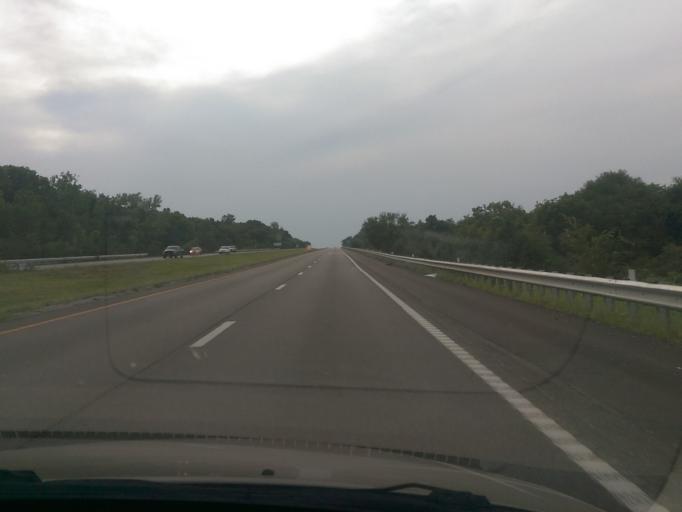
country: US
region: Missouri
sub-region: Andrew County
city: Savannah
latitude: 39.9042
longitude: -94.8853
